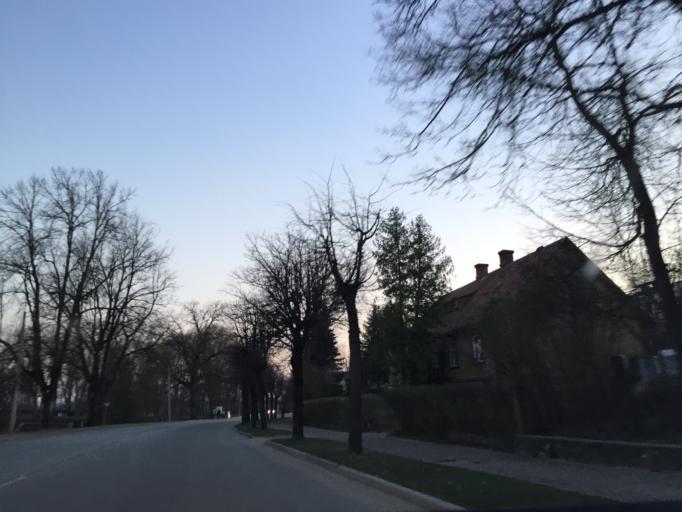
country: LV
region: Valkas Rajons
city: Valka
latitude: 57.7703
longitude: 26.0140
